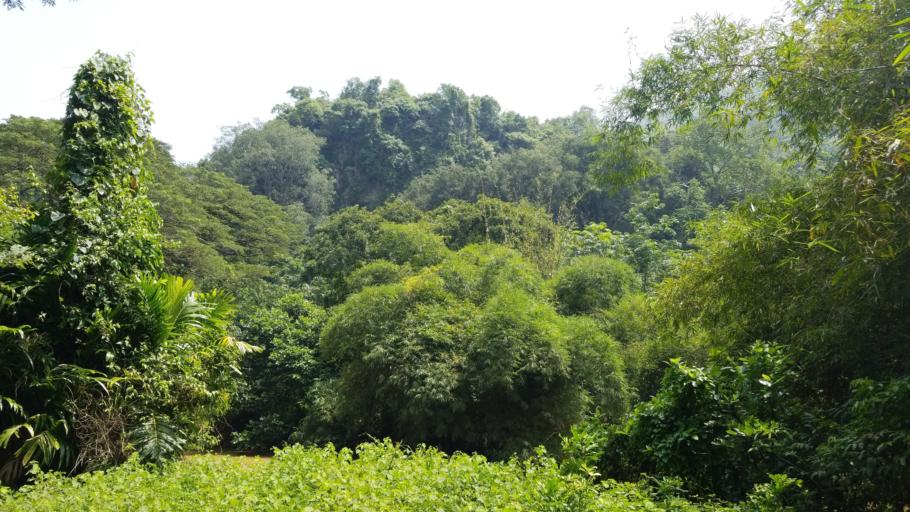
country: TH
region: Yala
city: Betong
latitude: 5.6632
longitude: 100.8867
